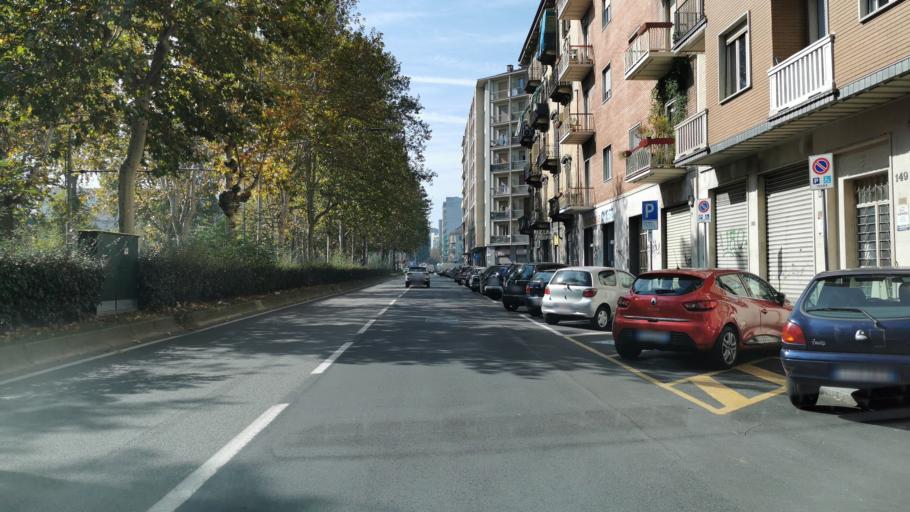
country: IT
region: Piedmont
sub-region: Provincia di Torino
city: Turin
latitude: 45.0888
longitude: 7.6586
